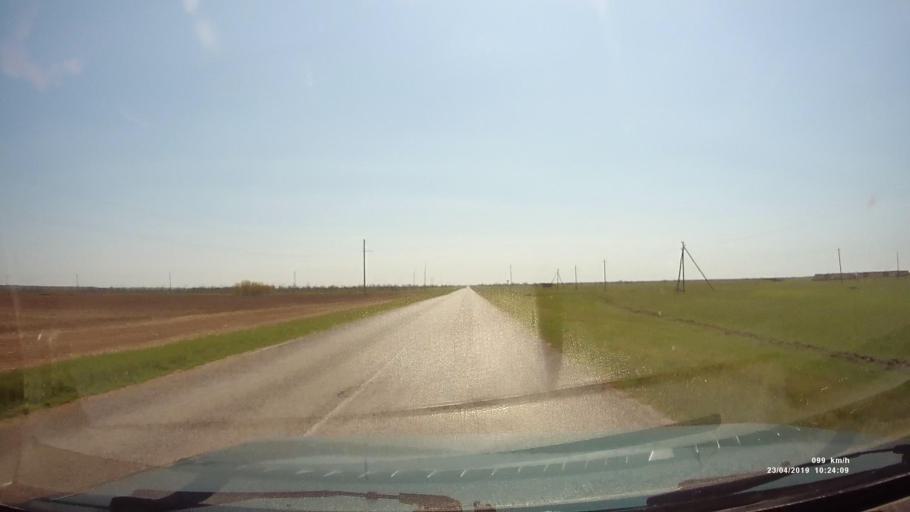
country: RU
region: Rostov
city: Sovetskoye
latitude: 46.6414
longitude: 42.4368
